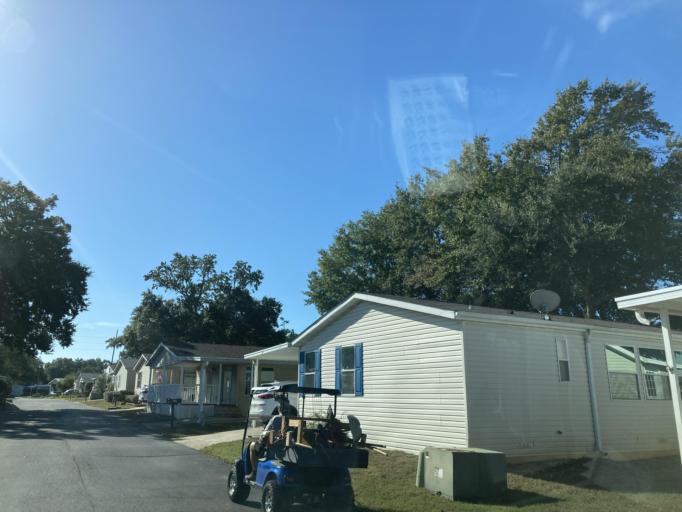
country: US
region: Mississippi
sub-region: Harrison County
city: D'Iberville
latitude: 30.4052
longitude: -88.9409
